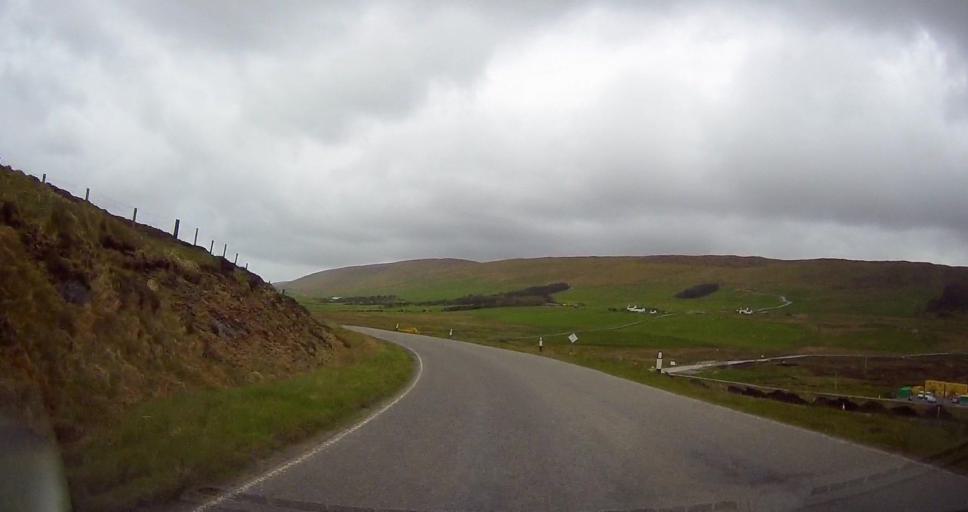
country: GB
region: Scotland
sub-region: Shetland Islands
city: Lerwick
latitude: 60.2782
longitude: -1.2711
